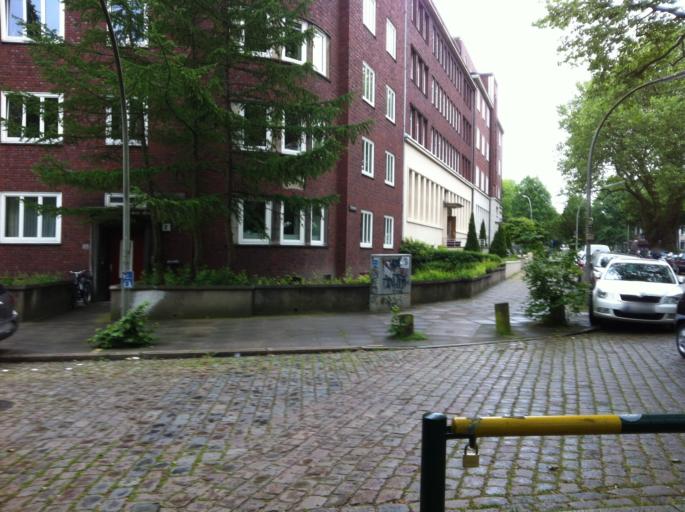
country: DE
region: Hamburg
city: Altona
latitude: 53.5547
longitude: 9.9389
